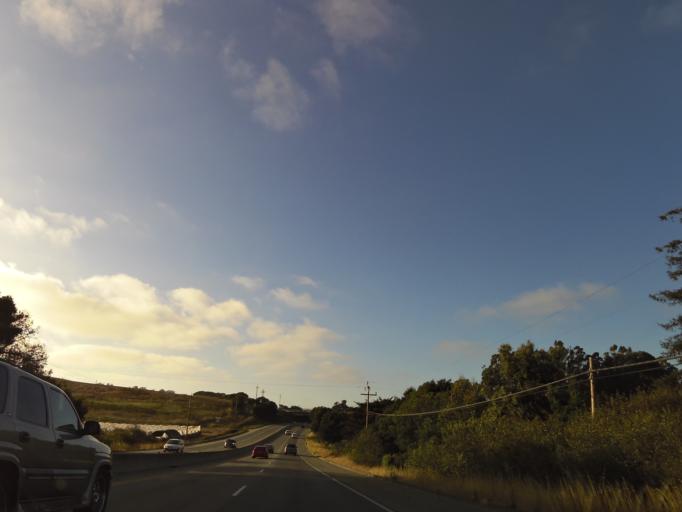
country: US
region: California
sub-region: Monterey County
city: Prunedale
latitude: 36.7660
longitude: -121.6681
